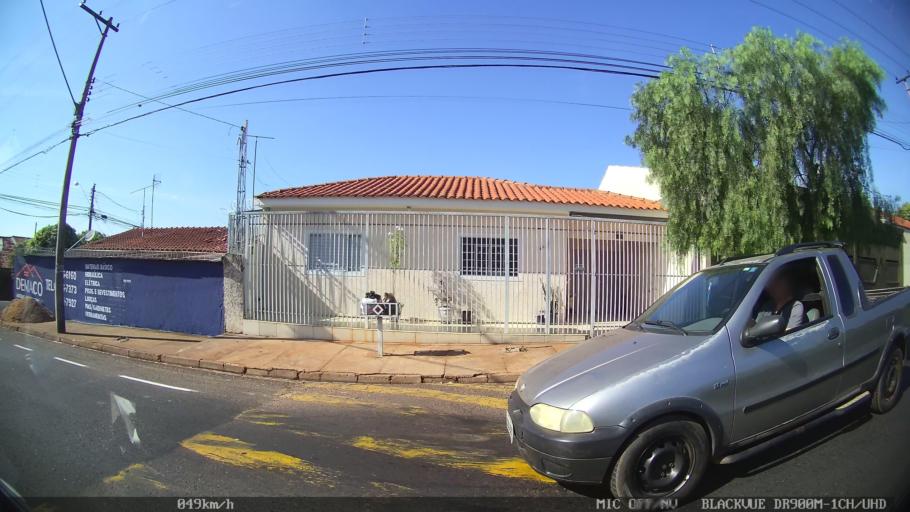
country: BR
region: Sao Paulo
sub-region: Sao Jose Do Rio Preto
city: Sao Jose do Rio Preto
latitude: -20.7780
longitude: -49.4011
